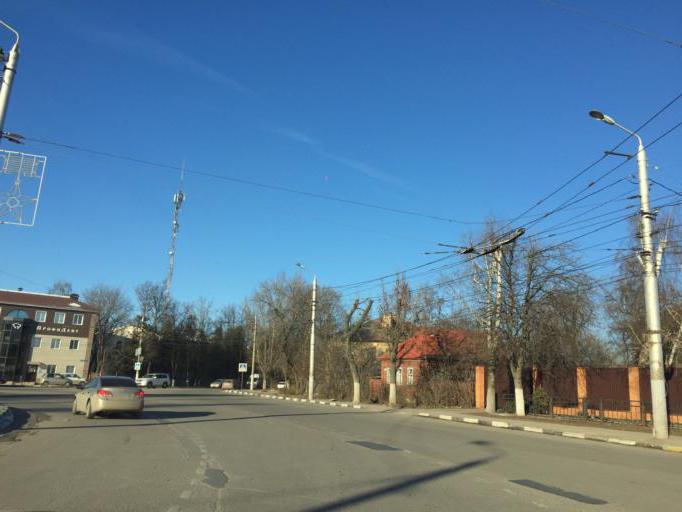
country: RU
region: Tula
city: Tula
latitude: 54.1857
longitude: 37.5728
